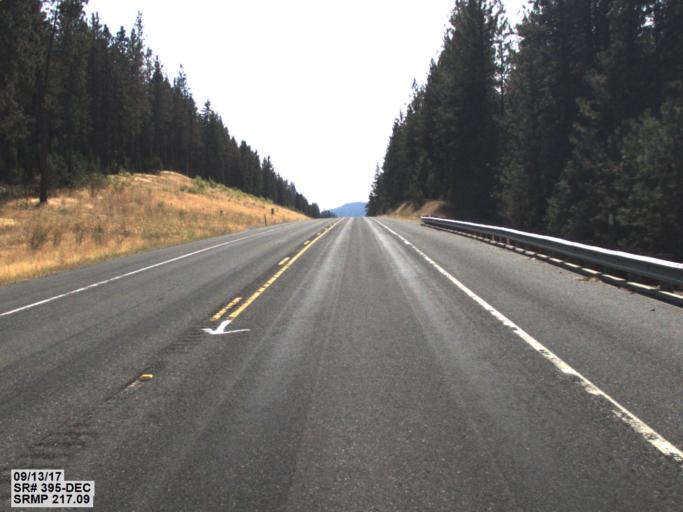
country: US
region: Washington
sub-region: Stevens County
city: Chewelah
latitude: 48.3749
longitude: -117.8396
